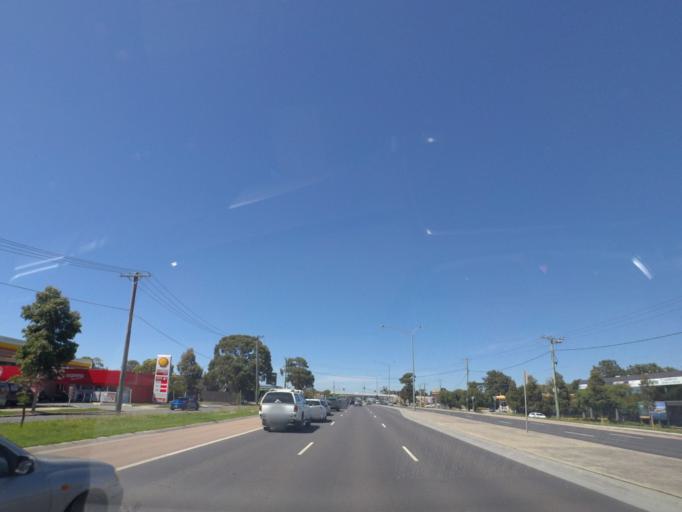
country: AU
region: Victoria
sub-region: Hume
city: Gladstone Park
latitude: -37.6865
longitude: 144.8827
